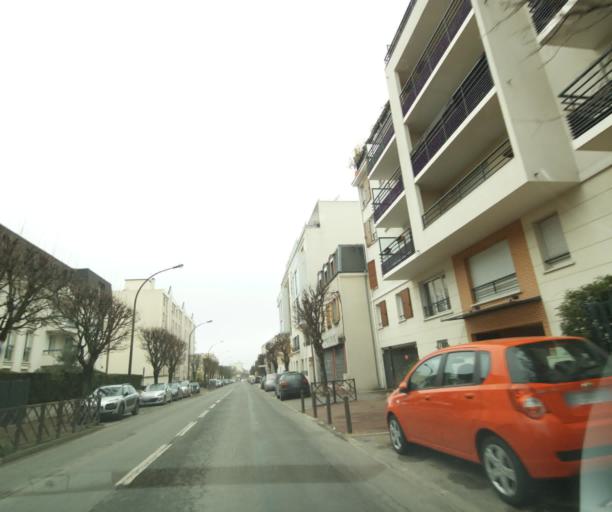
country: FR
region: Ile-de-France
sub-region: Departement de Seine-Saint-Denis
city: Livry-Gargan
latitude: 48.9276
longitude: 2.5435
